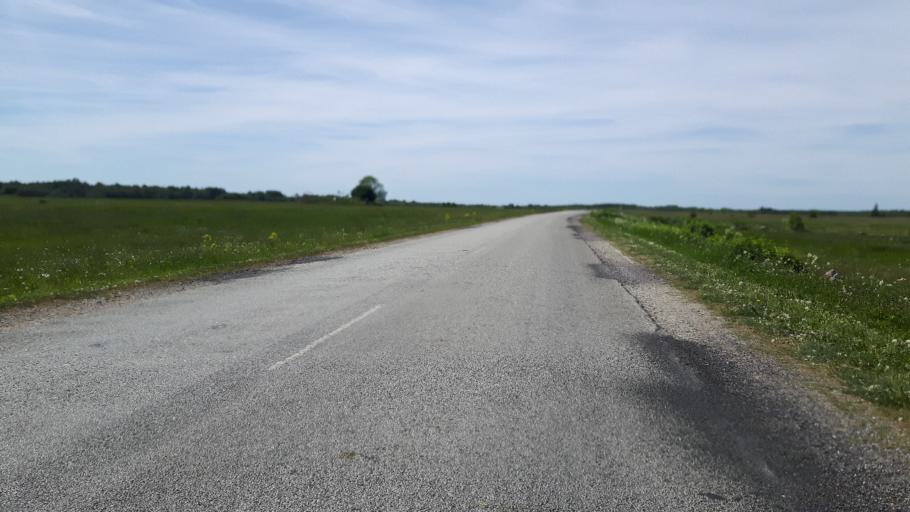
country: EE
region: Harju
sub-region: Kuusalu vald
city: Kuusalu
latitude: 59.4597
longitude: 25.3422
